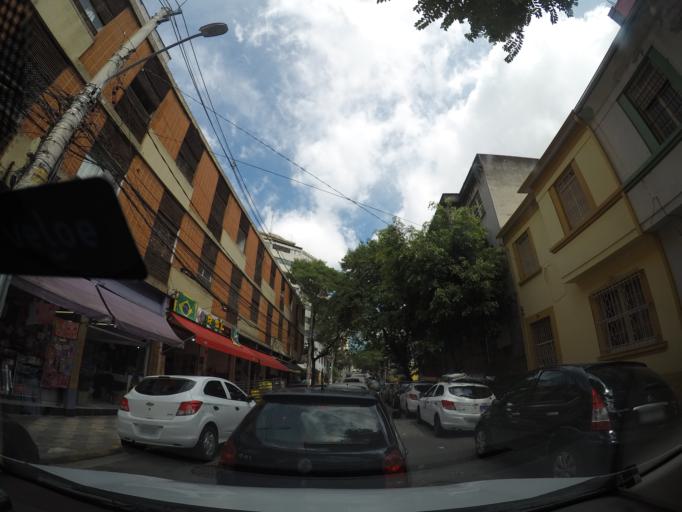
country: BR
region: Sao Paulo
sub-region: Sao Paulo
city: Sao Paulo
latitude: -23.5574
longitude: -46.6424
